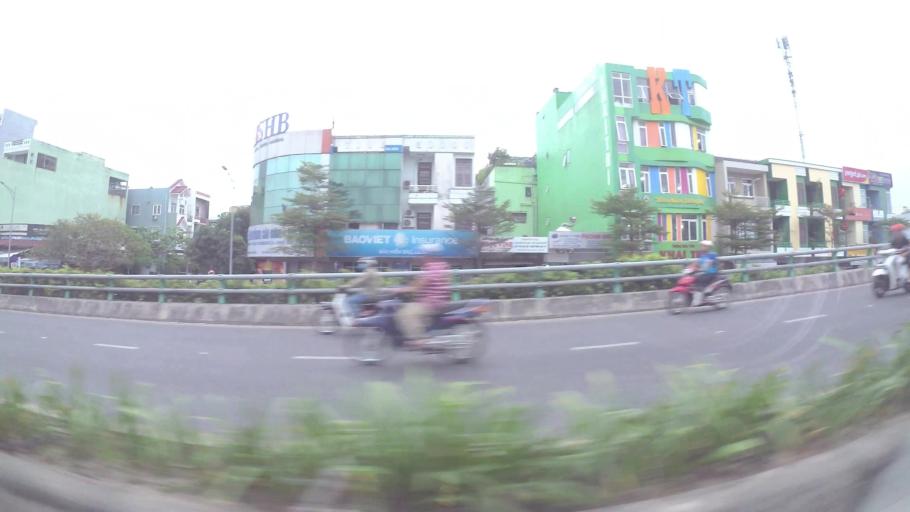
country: VN
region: Da Nang
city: Thanh Khe
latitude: 16.0637
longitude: 108.1813
